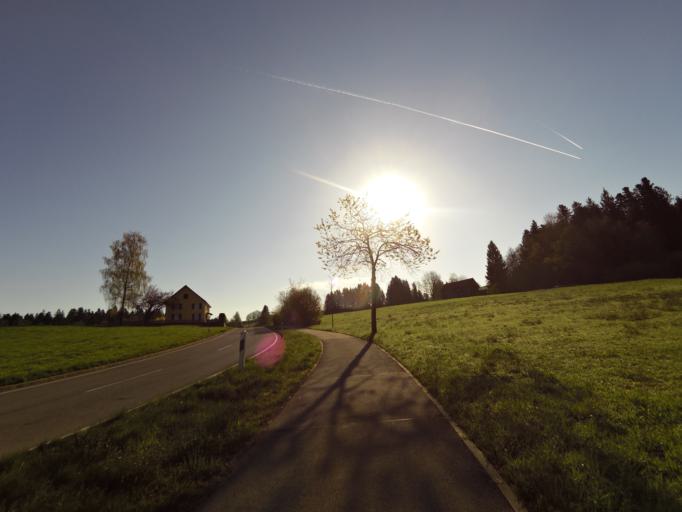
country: DE
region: Bavaria
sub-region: Swabia
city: Weiler-Simmerberg
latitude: 47.5845
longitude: 9.9269
